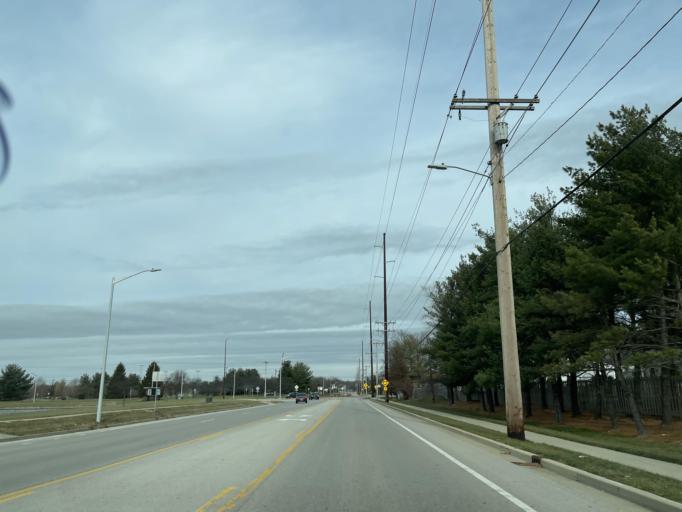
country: US
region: Illinois
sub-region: Sangamon County
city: Jerome
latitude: 39.7694
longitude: -89.7346
